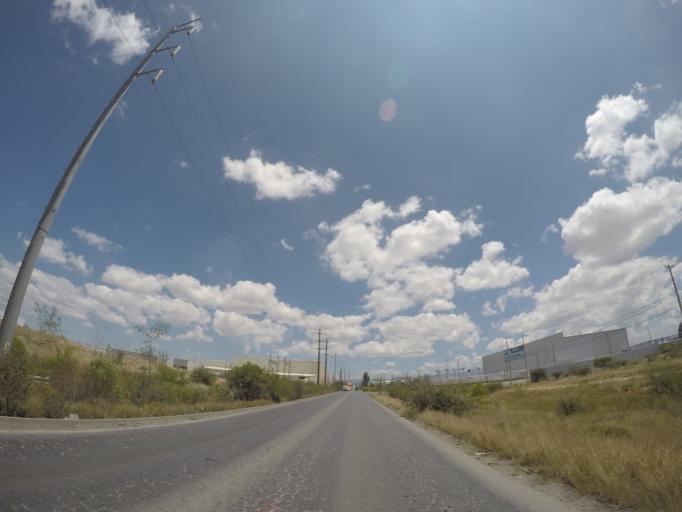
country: MX
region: San Luis Potosi
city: La Pila
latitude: 22.0473
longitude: -100.8738
